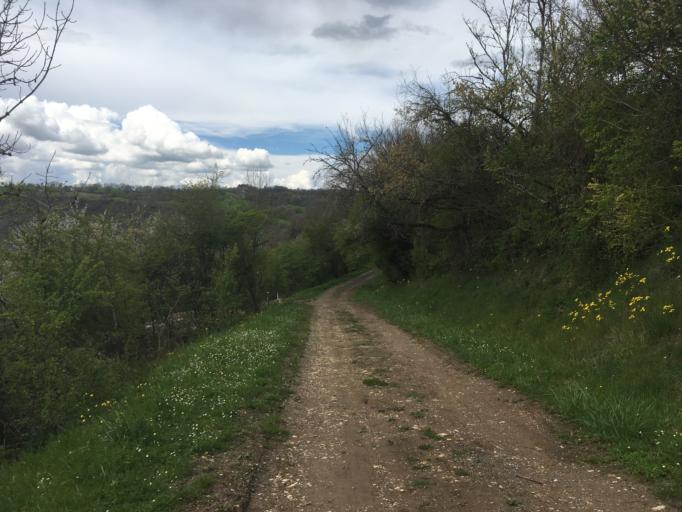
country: FR
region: Midi-Pyrenees
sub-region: Departement de l'Aveyron
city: Capdenac-Gare
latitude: 44.5788
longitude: 2.0692
